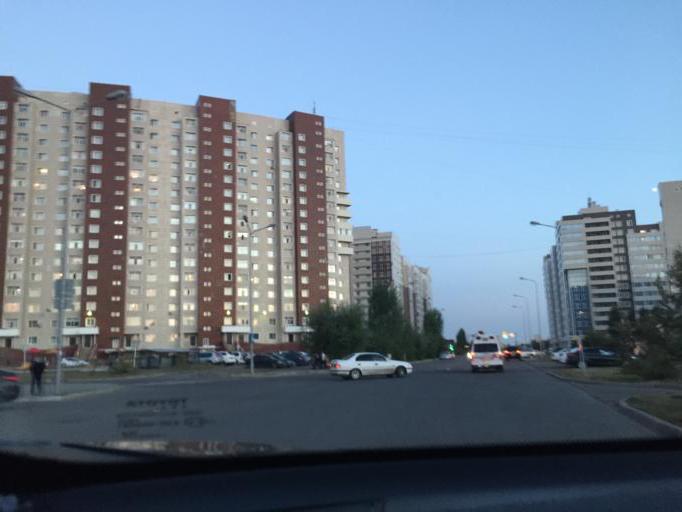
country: KZ
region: Astana Qalasy
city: Astana
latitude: 51.1426
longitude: 71.4810
